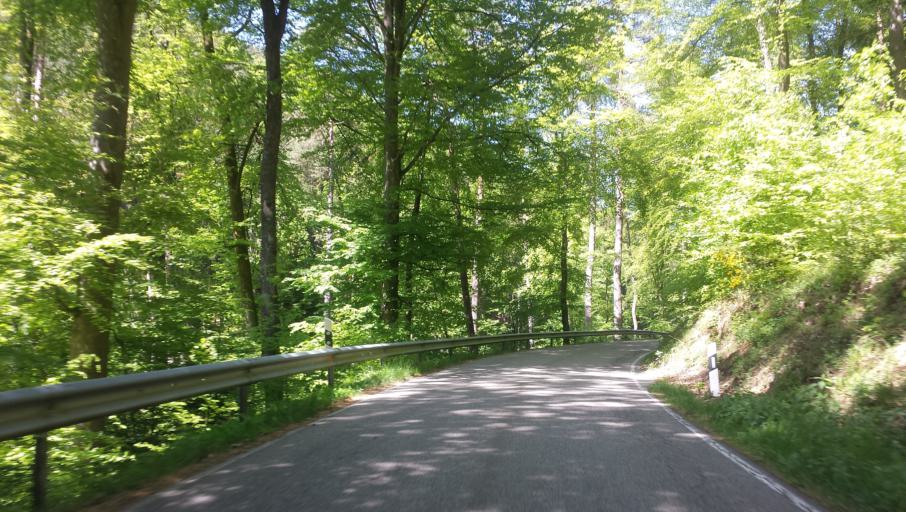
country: DE
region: Rheinland-Pfalz
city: Ramberg
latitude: 49.2873
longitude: 8.0145
